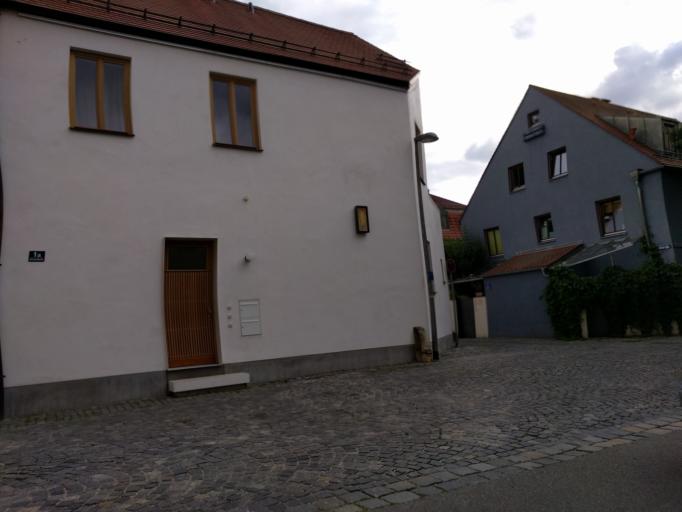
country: DE
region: Bavaria
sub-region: Upper Palatinate
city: Lappersdorf
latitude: 49.0250
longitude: 12.0945
